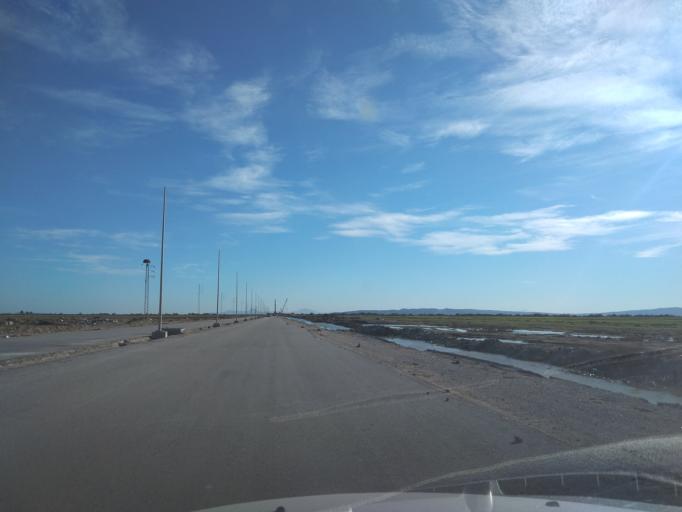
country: TN
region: Ariana
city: Qal'at al Andalus
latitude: 37.0311
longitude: 10.1360
